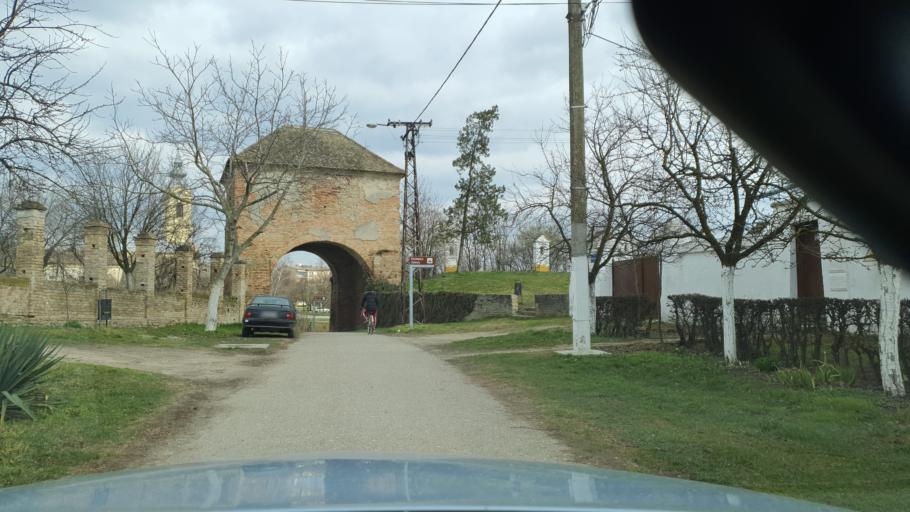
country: RS
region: Autonomna Pokrajina Vojvodina
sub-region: Juznobacki Okrug
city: Bac
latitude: 45.3921
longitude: 19.2253
